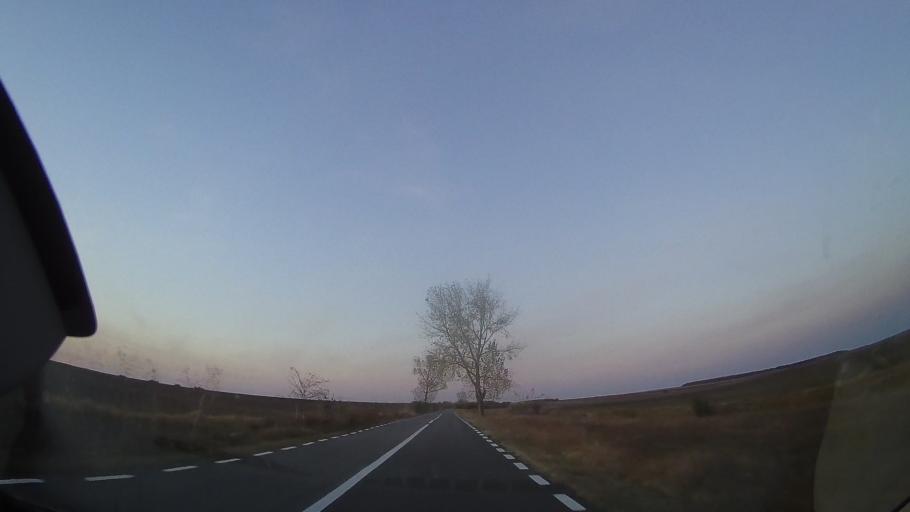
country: RO
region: Constanta
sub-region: Comuna Cobadin
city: Cobadin
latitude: 44.0277
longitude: 28.2628
